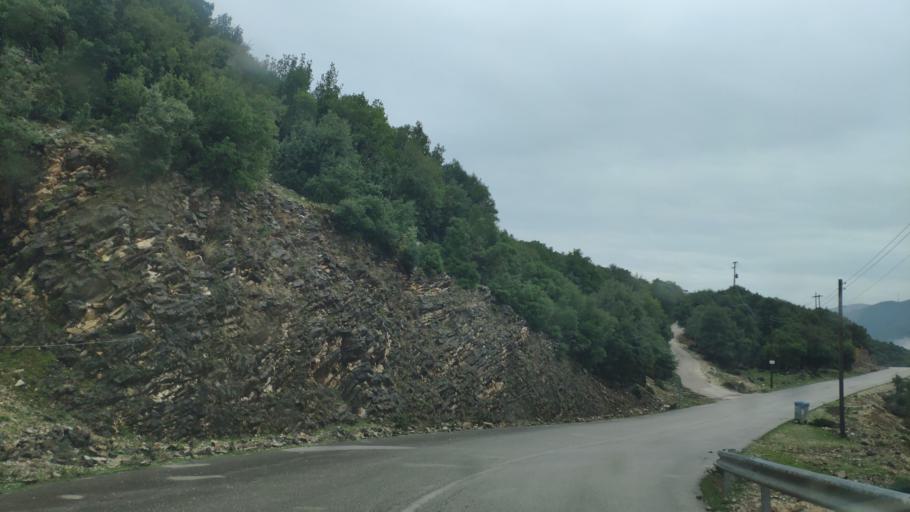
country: GR
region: Epirus
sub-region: Nomos Thesprotias
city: Paramythia
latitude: 39.3947
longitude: 20.6240
